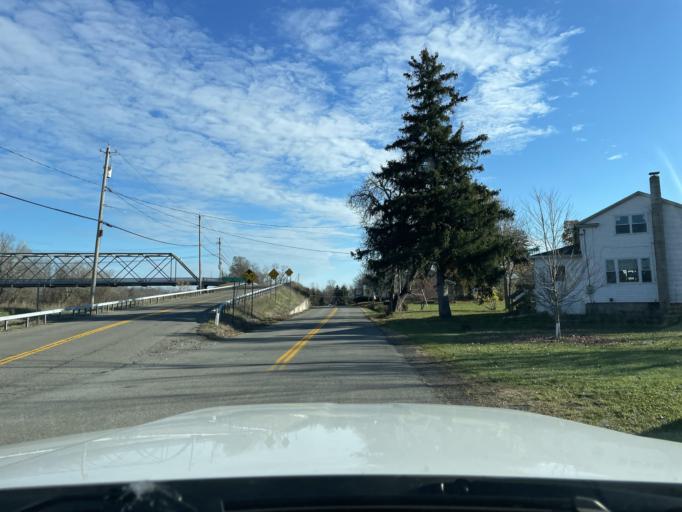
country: US
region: New York
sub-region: Niagara County
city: Gasport
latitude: 43.2059
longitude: -78.5469
